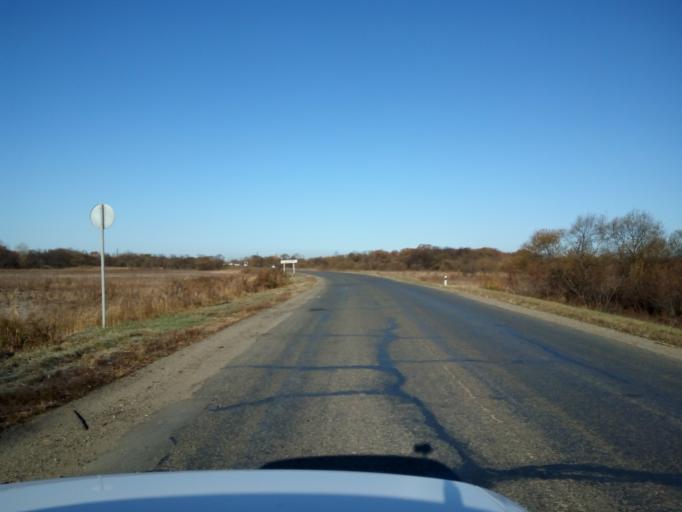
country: RU
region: Primorskiy
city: Dal'nerechensk
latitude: 45.9168
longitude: 133.7827
